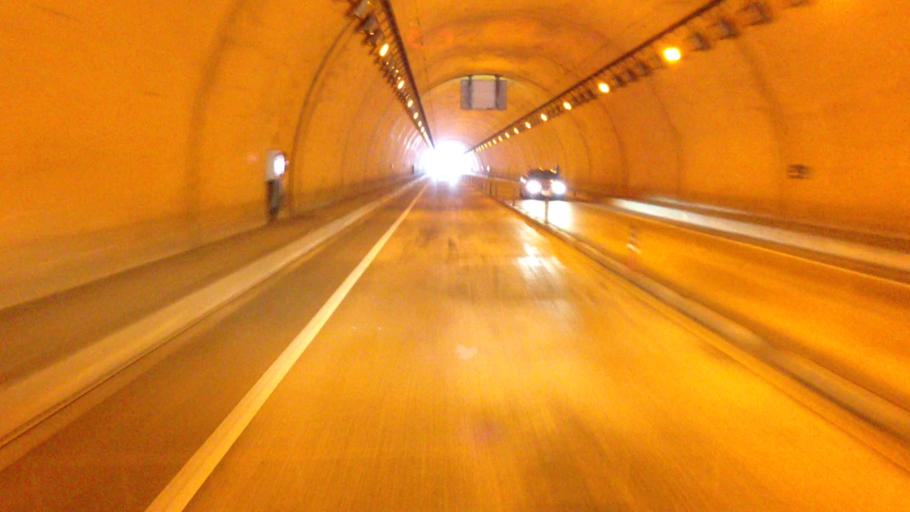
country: JP
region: Kanagawa
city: Yokosuka
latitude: 35.2408
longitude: 139.6538
